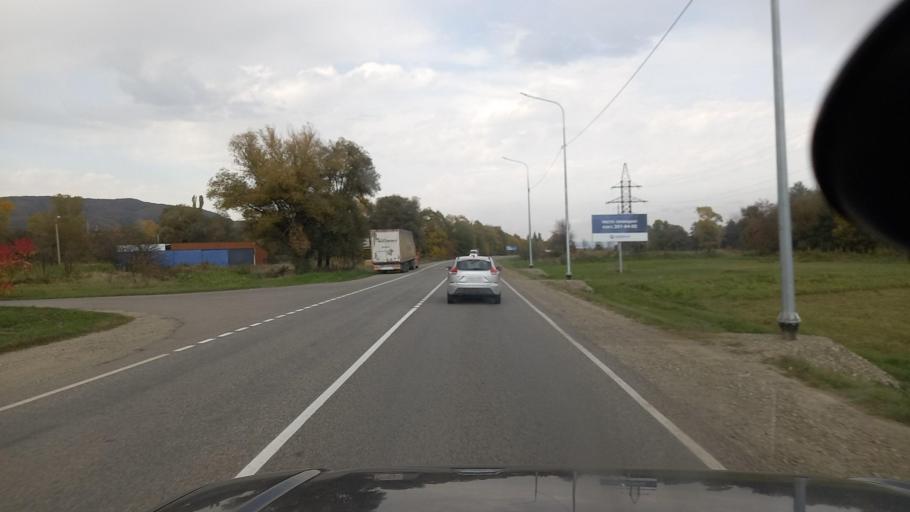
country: RU
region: Krasnodarskiy
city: Shedok
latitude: 44.1792
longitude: 40.8412
